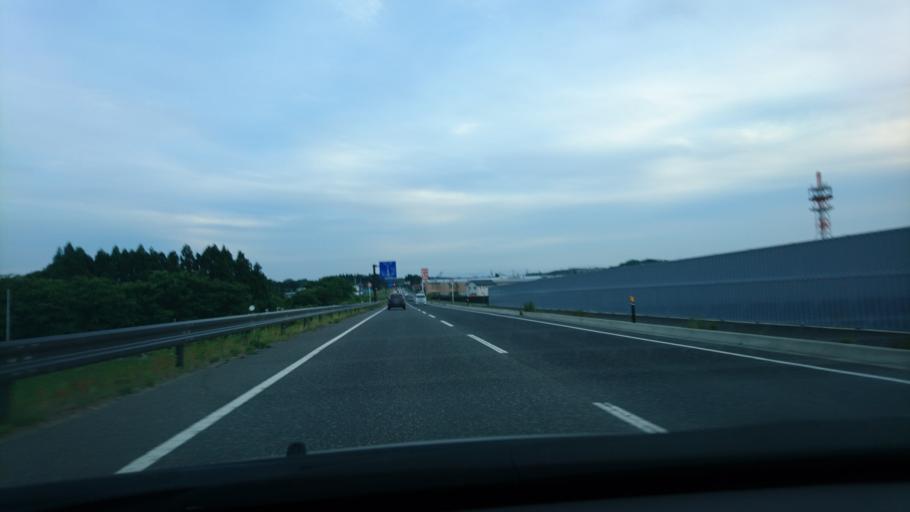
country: JP
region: Miyagi
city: Furukawa
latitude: 38.7369
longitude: 141.0372
